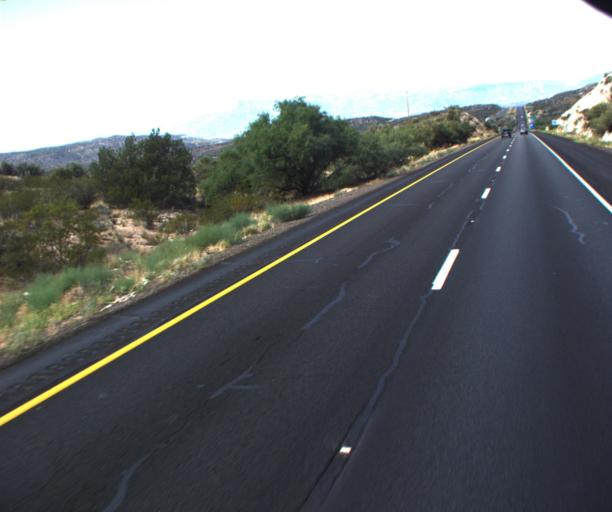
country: US
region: Arizona
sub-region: Yavapai County
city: Lake Montezuma
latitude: 34.6311
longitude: -111.8351
